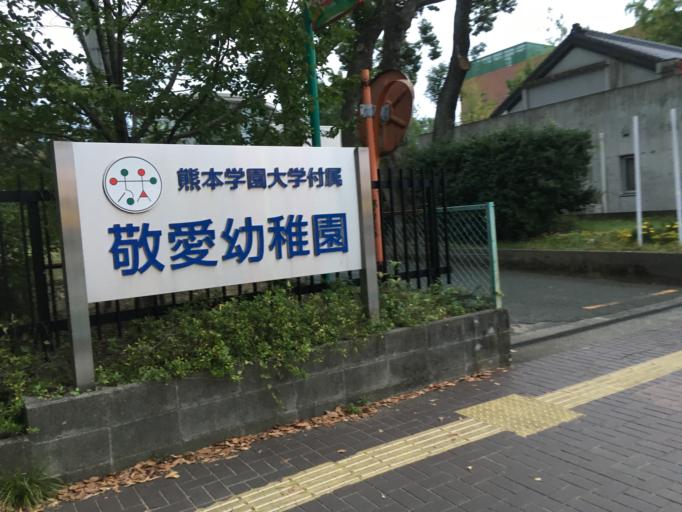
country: JP
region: Kumamoto
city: Kumamoto
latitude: 32.8038
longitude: 130.7264
